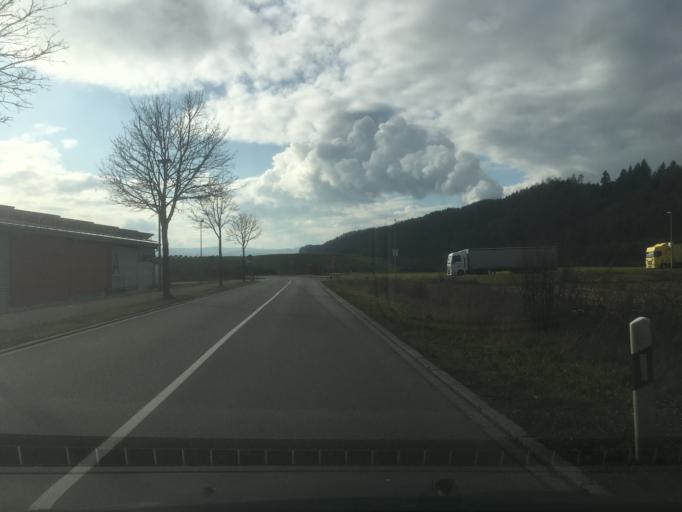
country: CH
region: Aargau
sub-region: Bezirk Zurzach
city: Koblenz
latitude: 47.6234
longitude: 8.2498
